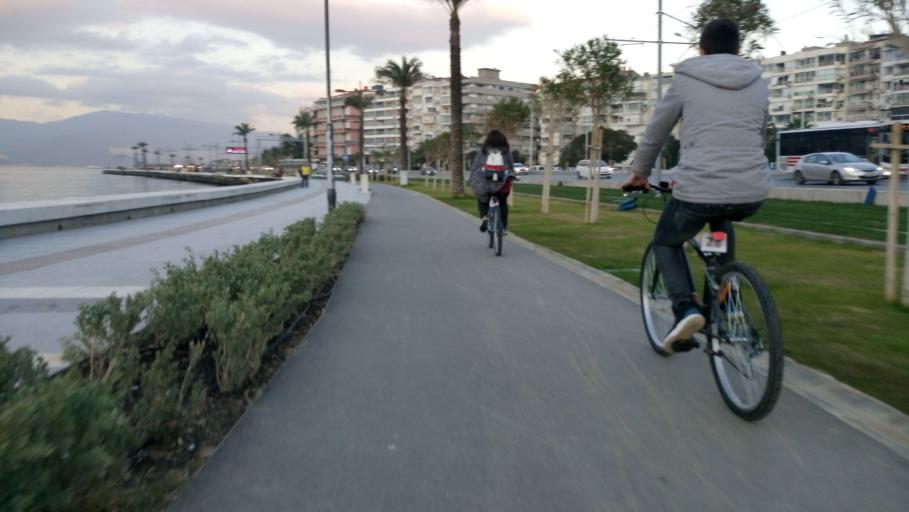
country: TR
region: Izmir
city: Izmir
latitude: 38.4110
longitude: 27.1195
